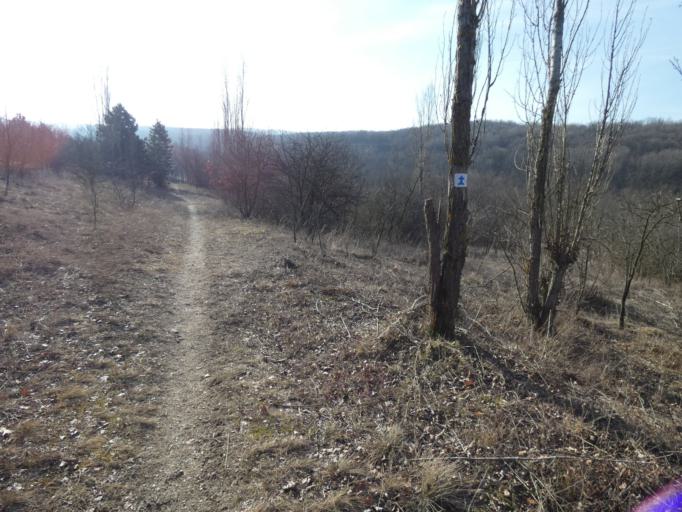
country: HU
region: Pest
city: Piliscsaba
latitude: 47.6212
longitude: 18.8405
